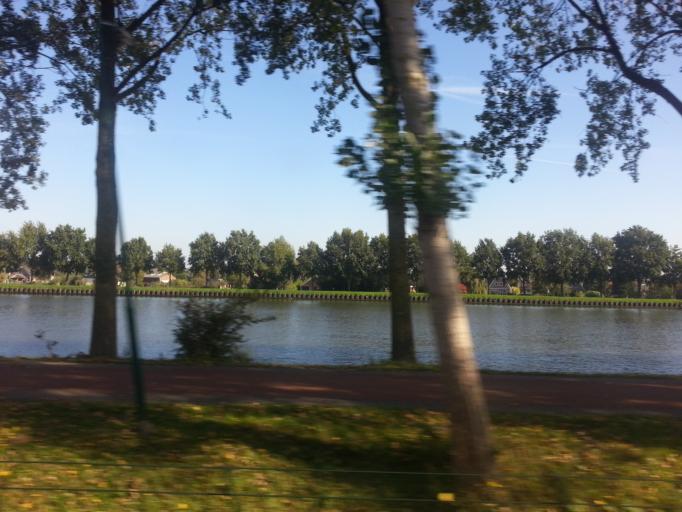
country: NL
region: Utrecht
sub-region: Stichtse Vecht
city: Spechtenkamp
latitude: 52.1462
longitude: 5.0159
